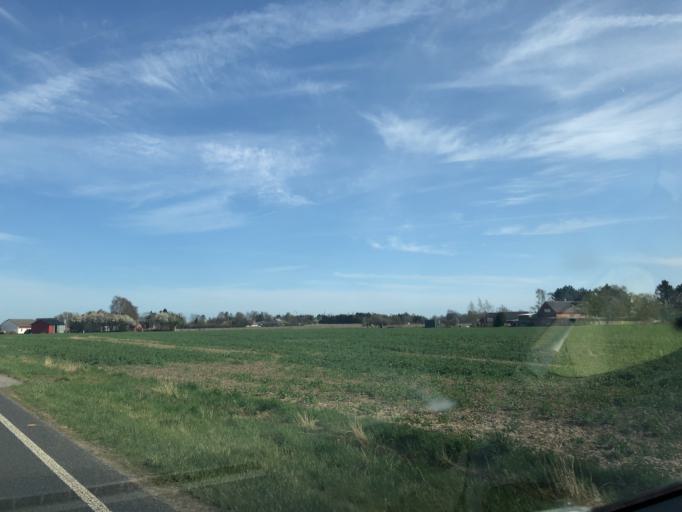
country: DK
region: Zealand
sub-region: Stevns Kommune
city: Harlev
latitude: 55.2779
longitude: 12.2502
